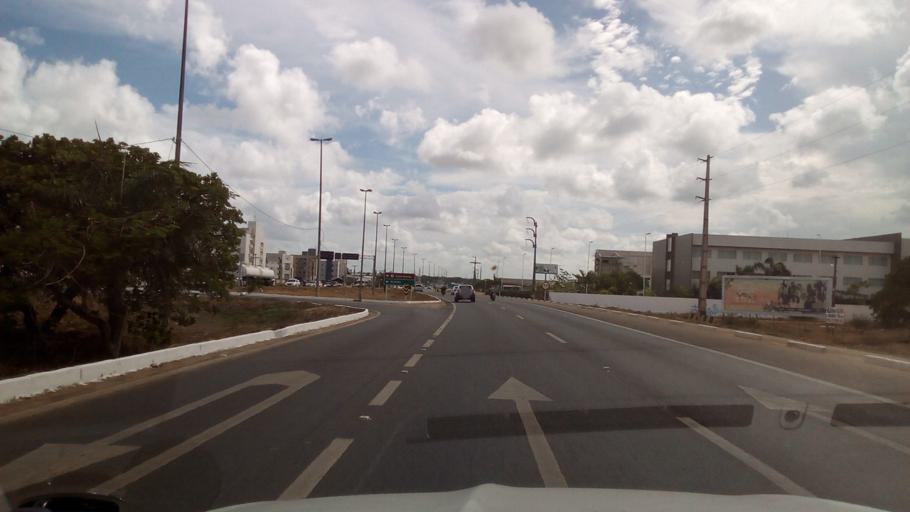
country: BR
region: Paraiba
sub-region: Cabedelo
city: Cabedelo
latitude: -7.0438
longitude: -34.8468
